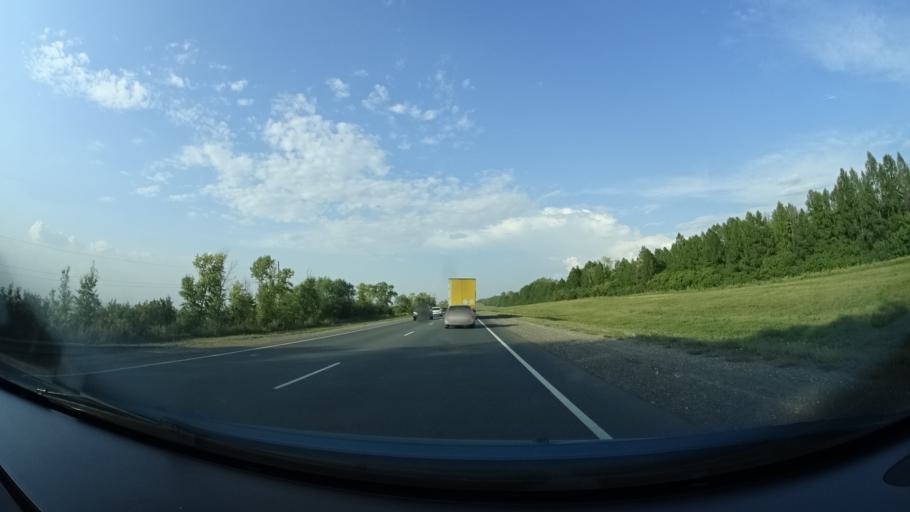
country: RU
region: Samara
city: Krasnyy Yar
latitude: 53.6528
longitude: 50.7447
